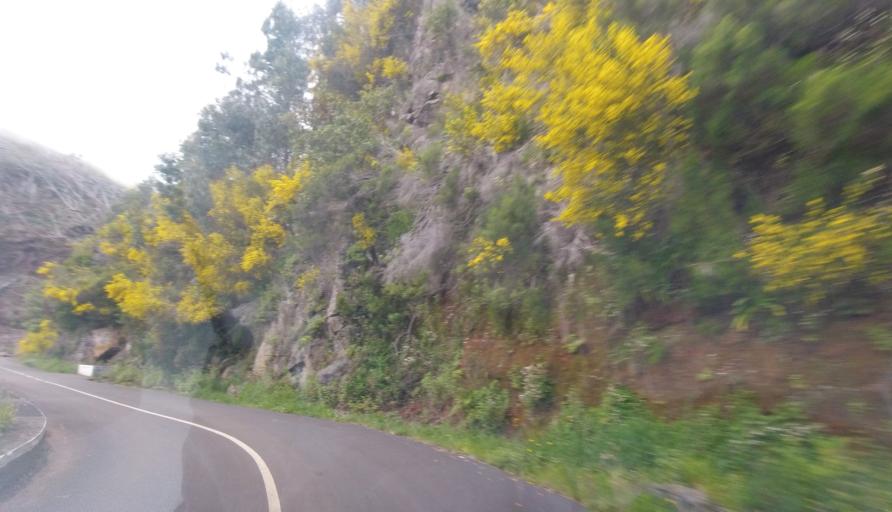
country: PT
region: Madeira
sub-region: Funchal
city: Nossa Senhora do Monte
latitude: 32.6928
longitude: -16.8957
